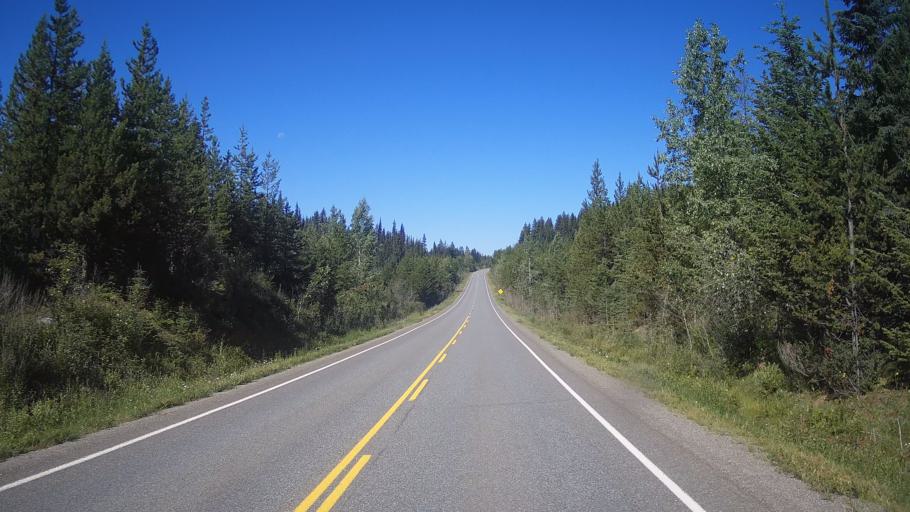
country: CA
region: British Columbia
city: Kamloops
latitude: 51.4969
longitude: -120.3820
